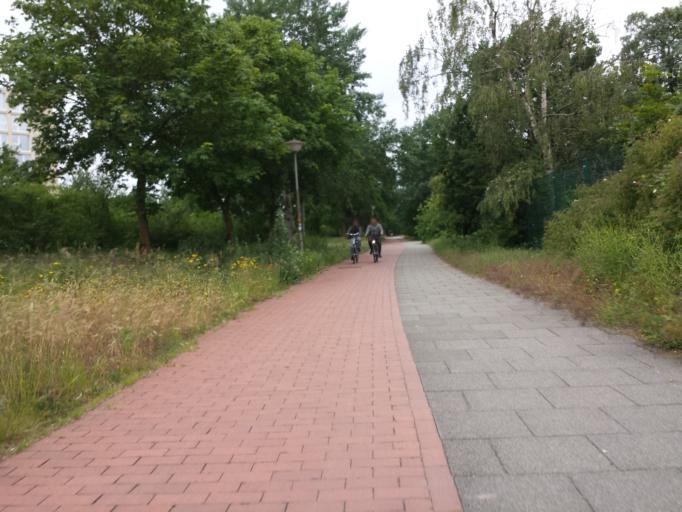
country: DE
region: Bremen
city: Bremen
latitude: 53.1062
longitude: 8.8602
